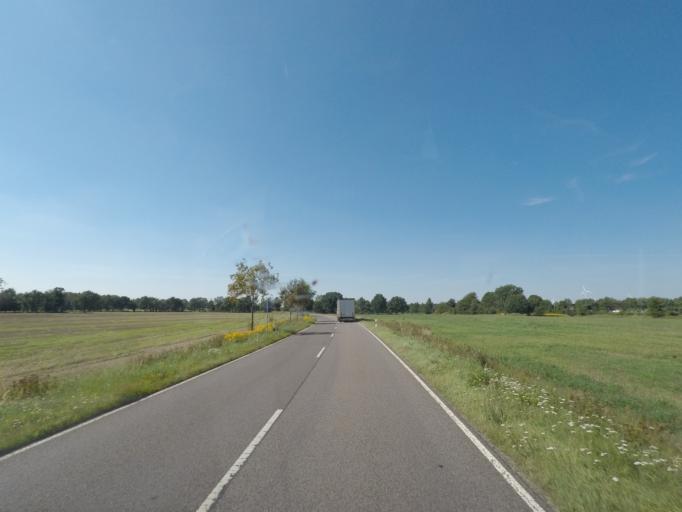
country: DE
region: Brandenburg
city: Welzow
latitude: 51.5737
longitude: 14.0936
